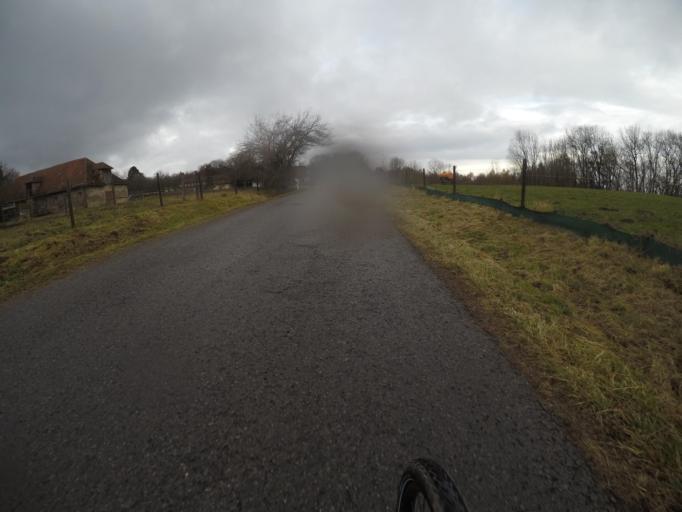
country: DE
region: Baden-Wuerttemberg
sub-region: Regierungsbezirk Stuttgart
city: Gerlingen
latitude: 48.7858
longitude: 9.0896
